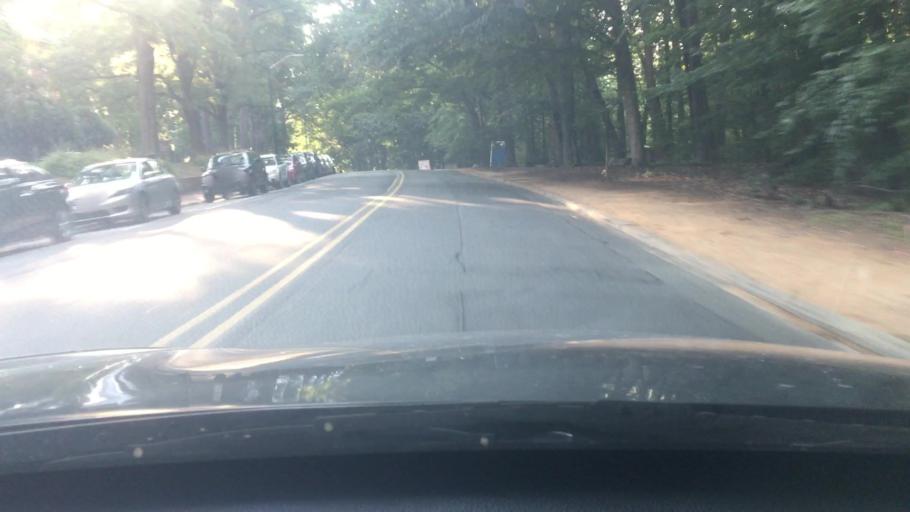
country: US
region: North Carolina
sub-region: Orange County
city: Chapel Hill
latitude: 35.9126
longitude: -79.0438
